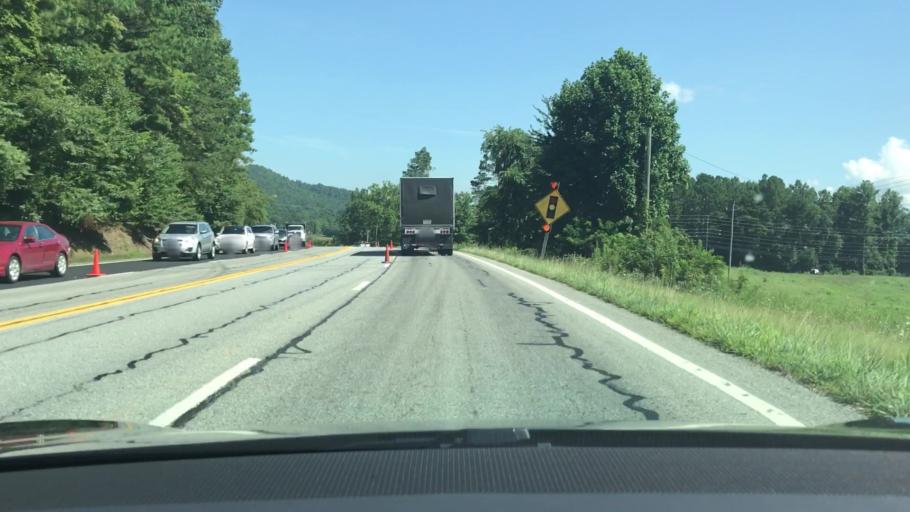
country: US
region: Georgia
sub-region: Rabun County
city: Mountain City
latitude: 34.9552
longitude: -83.3861
